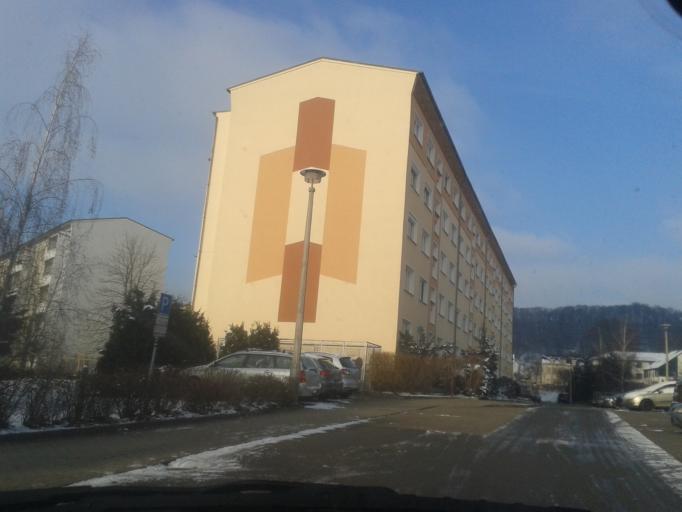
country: DE
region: Saxony
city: Radebeul
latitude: 51.1040
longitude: 13.6888
